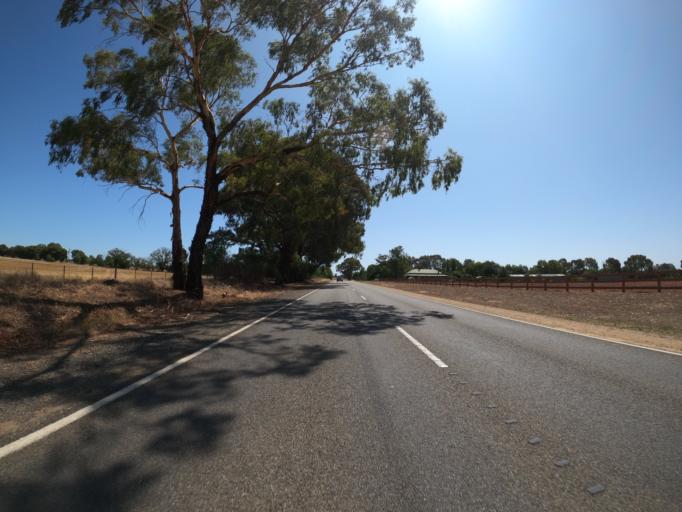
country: AU
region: Victoria
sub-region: Moira
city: Yarrawonga
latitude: -36.0257
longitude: 146.0953
